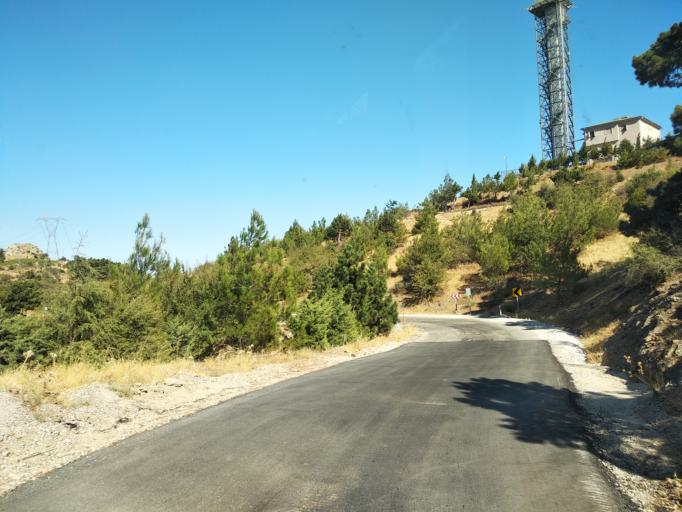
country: TR
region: Izmir
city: Gaziemir
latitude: 38.3118
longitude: 26.9998
